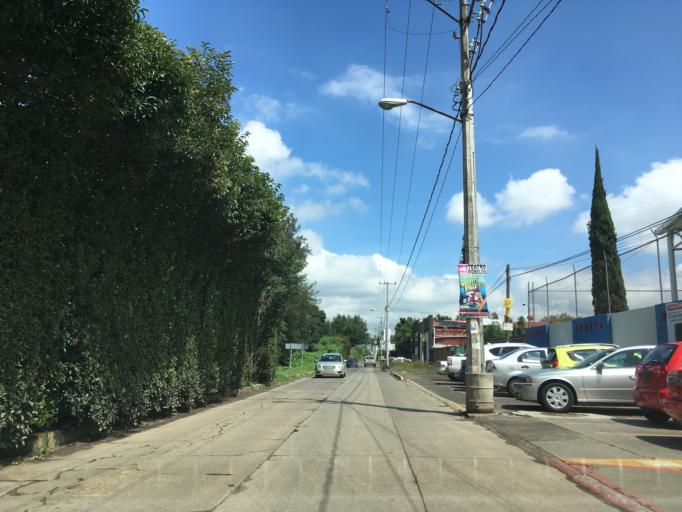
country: MX
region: Michoacan
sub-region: Morelia
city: Morelos
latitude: 19.6756
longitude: -101.2356
